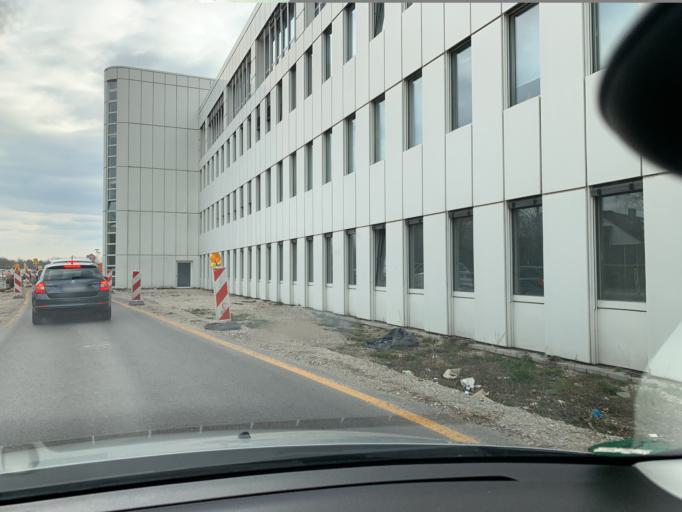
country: DE
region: Bavaria
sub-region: Upper Bavaria
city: Unterschleissheim
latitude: 48.2755
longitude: 11.5618
